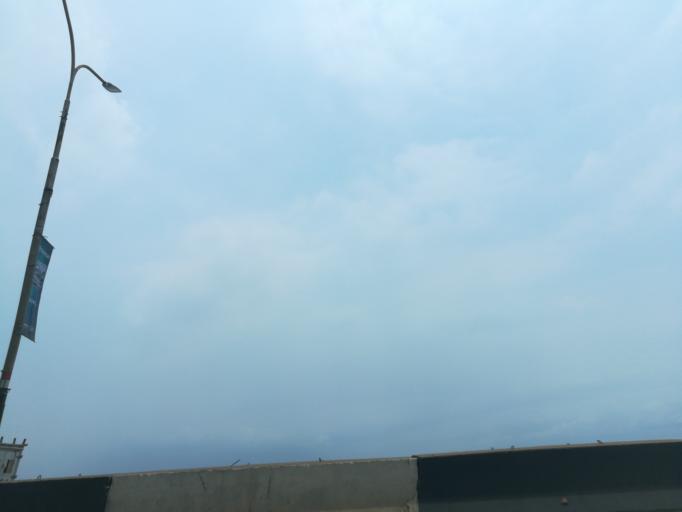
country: NG
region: Lagos
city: Makoko
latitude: 6.5222
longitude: 3.4046
